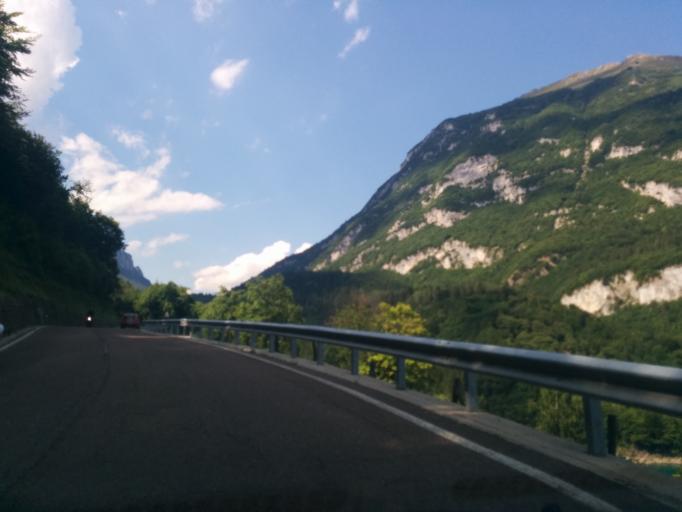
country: IT
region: Trentino-Alto Adige
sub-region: Provincia di Trento
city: Tenno
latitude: 45.9381
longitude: 10.8116
